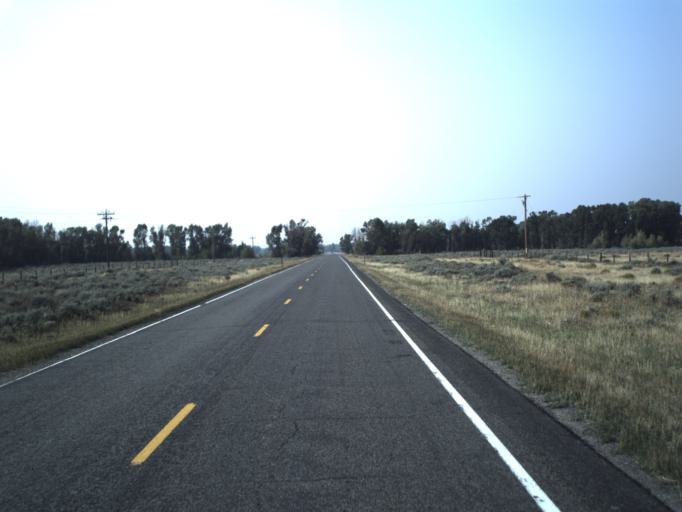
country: US
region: Wyoming
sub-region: Uinta County
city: Evanston
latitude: 40.9916
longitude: -110.8615
